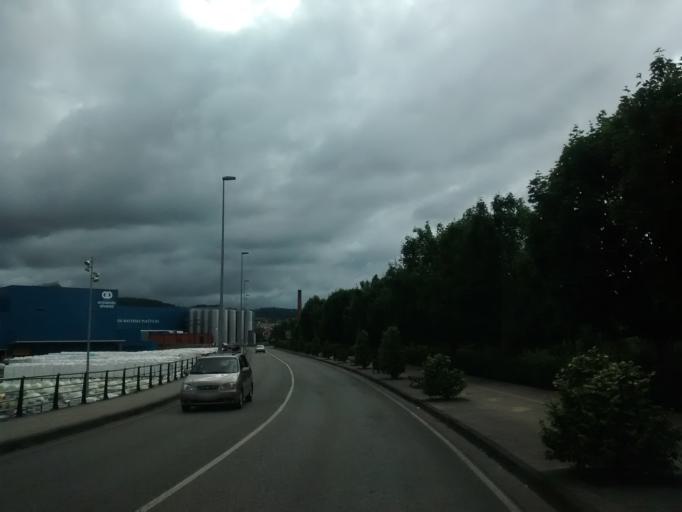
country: ES
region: Cantabria
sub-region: Provincia de Cantabria
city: Torrelavega
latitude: 43.3569
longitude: -4.0481
